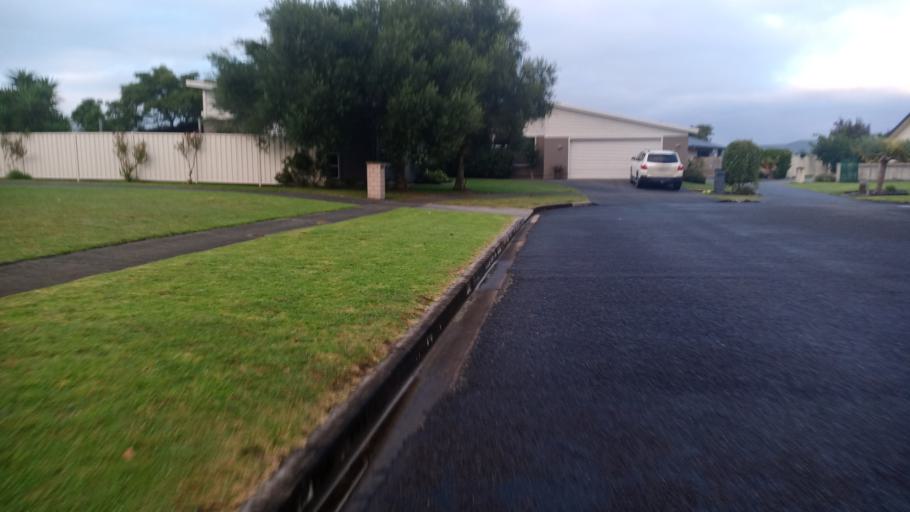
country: NZ
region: Gisborne
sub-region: Gisborne District
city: Gisborne
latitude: -38.6397
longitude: 177.9954
